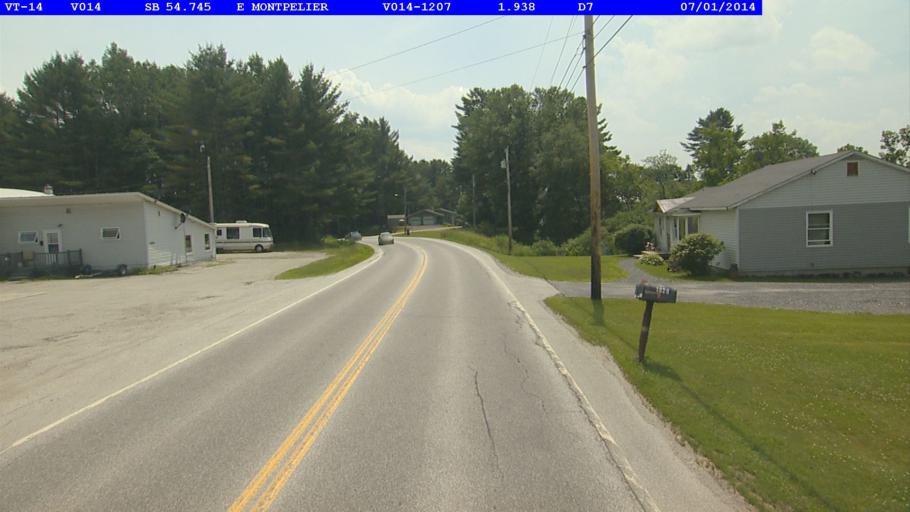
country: US
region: Vermont
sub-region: Washington County
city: Barre
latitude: 44.2614
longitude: -72.4878
